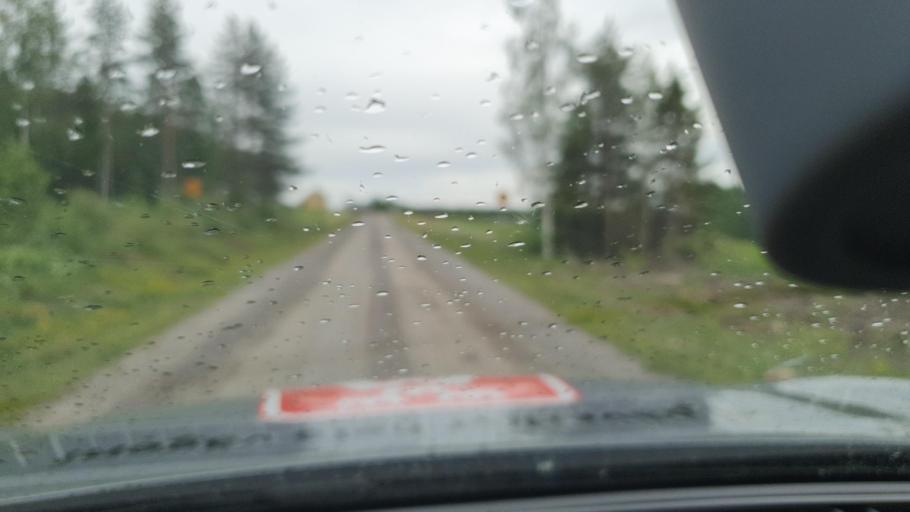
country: SE
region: Norrbotten
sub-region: Kalix Kommun
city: Rolfs
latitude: 66.0454
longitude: 23.0393
